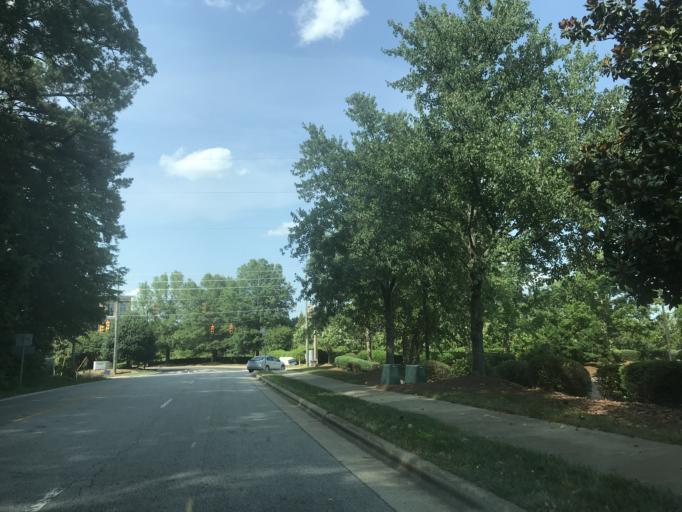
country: US
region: North Carolina
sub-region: Wake County
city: Cary
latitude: 35.8009
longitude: -78.7318
